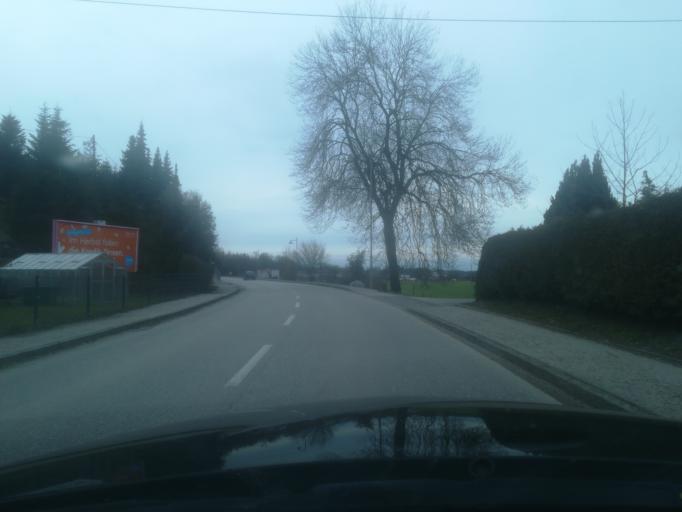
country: AT
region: Upper Austria
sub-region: Wels-Land
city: Gunskirchen
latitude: 48.0802
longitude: 13.9560
